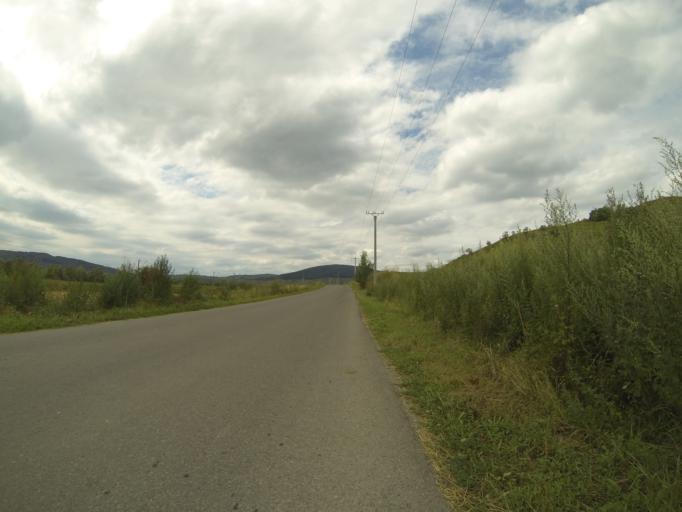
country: RO
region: Brasov
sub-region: Comuna Hoghiz
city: Hoghiz
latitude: 46.0287
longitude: 25.3859
